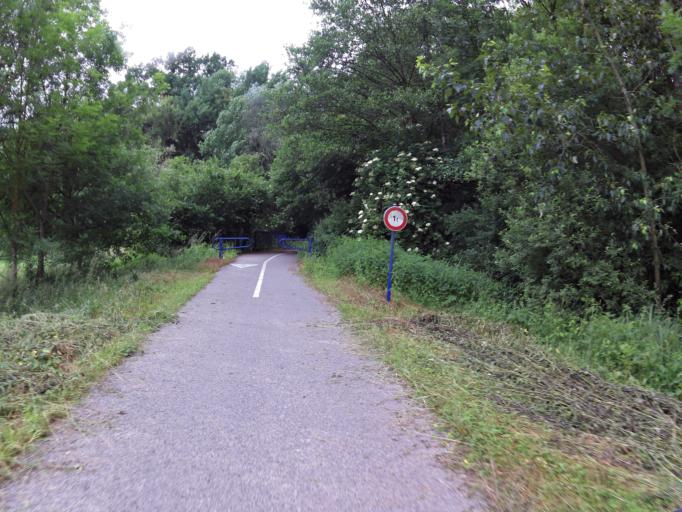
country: FR
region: Champagne-Ardenne
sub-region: Departement de la Haute-Marne
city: Montier-en-Der
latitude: 48.5236
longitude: 4.7700
